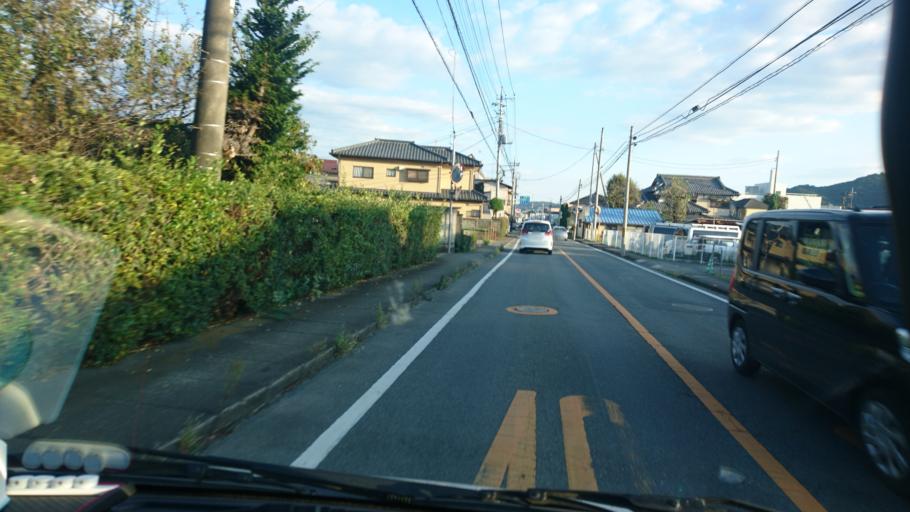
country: JP
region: Gunma
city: Kiryu
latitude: 36.3977
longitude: 139.3230
